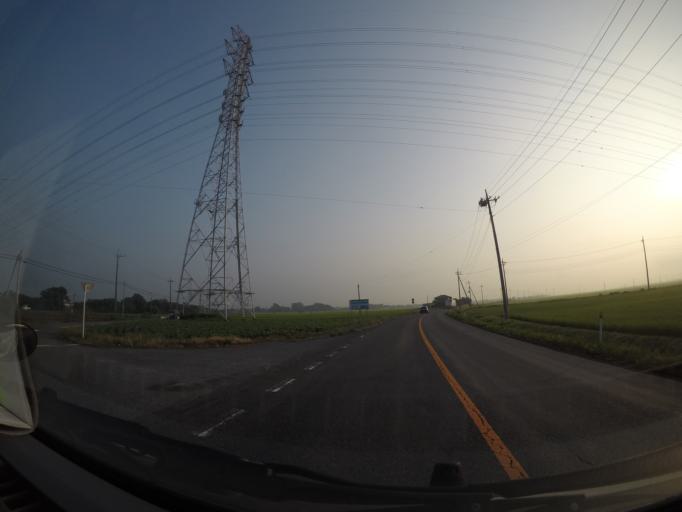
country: JP
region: Tochigi
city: Fujioka
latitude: 36.2598
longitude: 139.7094
